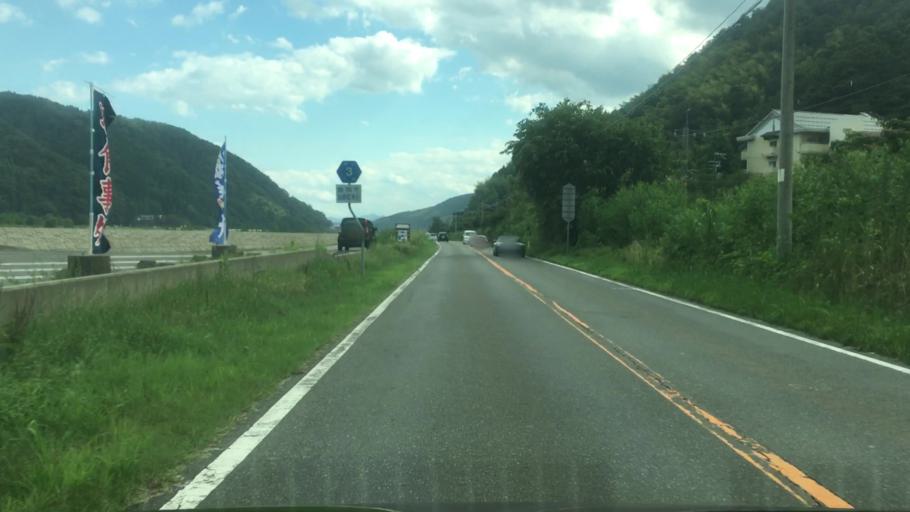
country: JP
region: Hyogo
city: Toyooka
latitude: 35.6027
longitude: 134.8017
